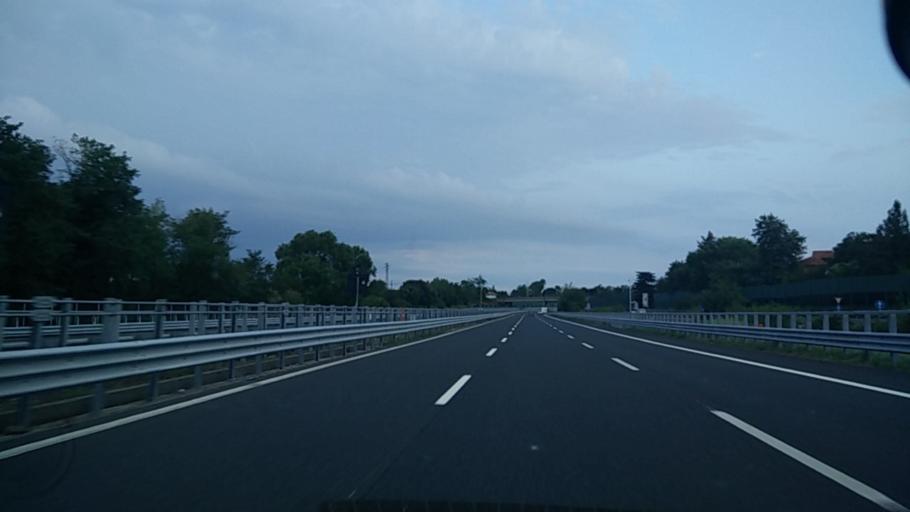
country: IT
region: Friuli Venezia Giulia
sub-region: Provincia di Udine
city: Passons
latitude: 46.0780
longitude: 13.1929
